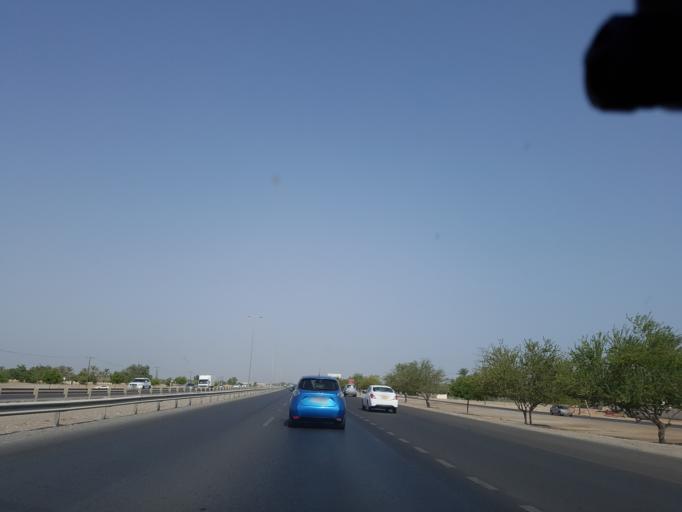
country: OM
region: Al Batinah
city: Barka'
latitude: 23.7232
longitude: 57.7311
